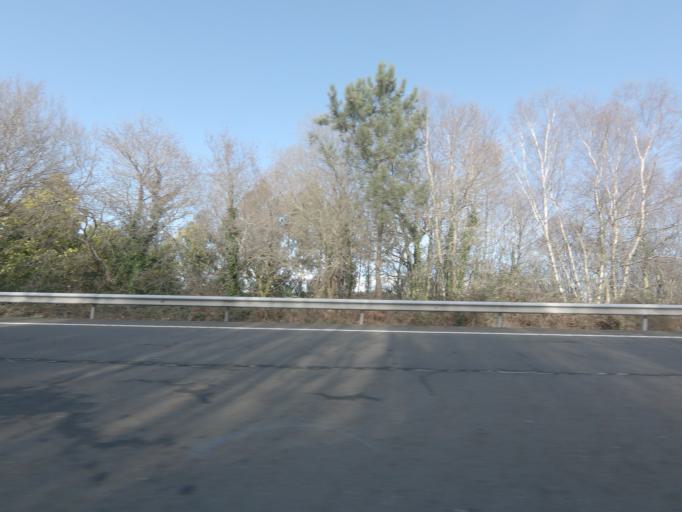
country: ES
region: Galicia
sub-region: Provincia da Coruna
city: Ribeira
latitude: 42.7144
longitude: -8.3602
